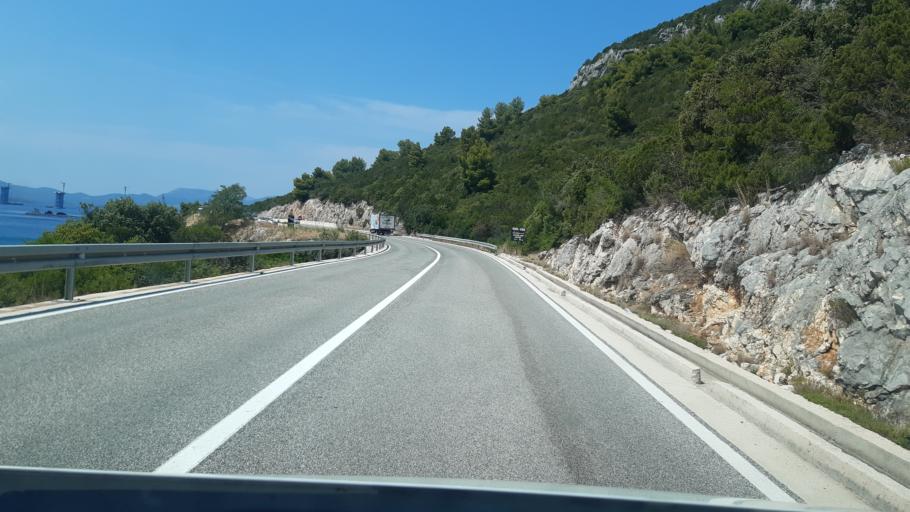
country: BA
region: Federation of Bosnia and Herzegovina
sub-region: Hercegovacko-Bosanski Kanton
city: Neum
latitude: 42.9421
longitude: 17.5717
